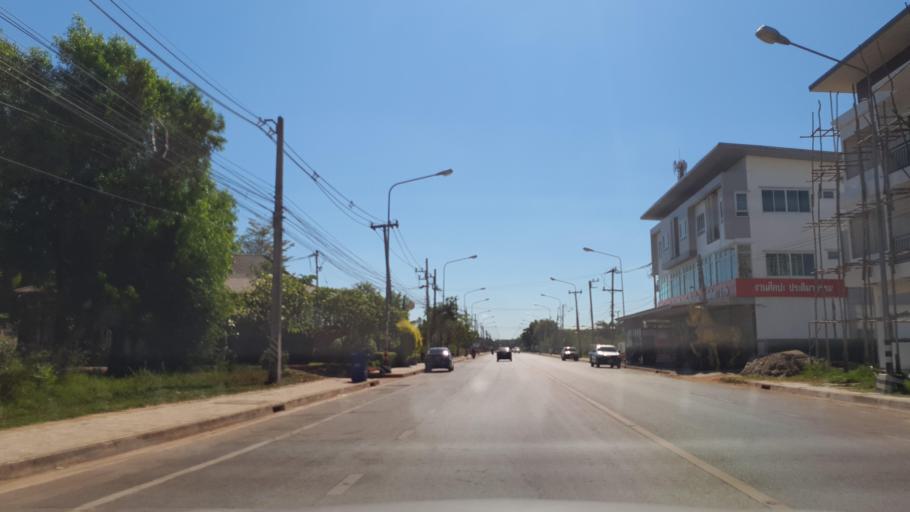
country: TH
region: Sakon Nakhon
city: Sakon Nakhon
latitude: 17.1545
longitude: 104.1272
